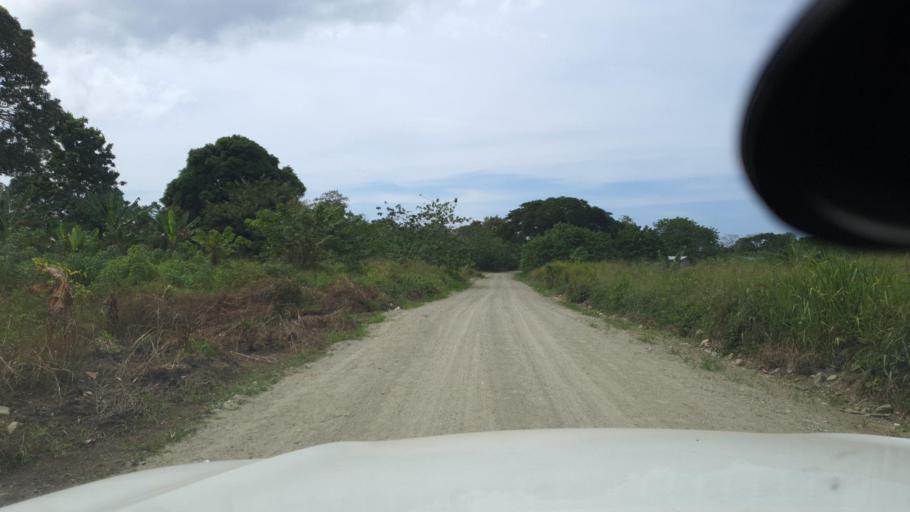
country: SB
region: Guadalcanal
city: Honiara
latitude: -9.4165
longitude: 159.8880
